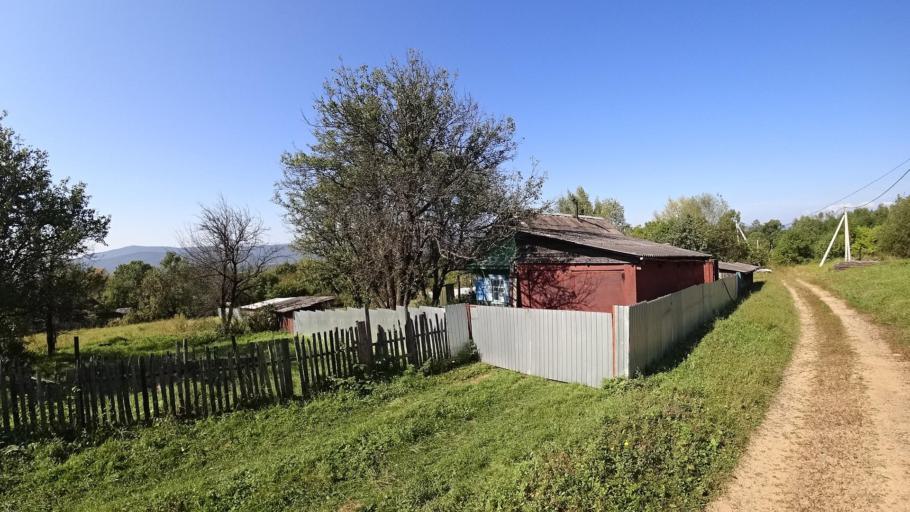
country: RU
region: Jewish Autonomous Oblast
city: Bira
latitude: 49.0069
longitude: 132.4671
